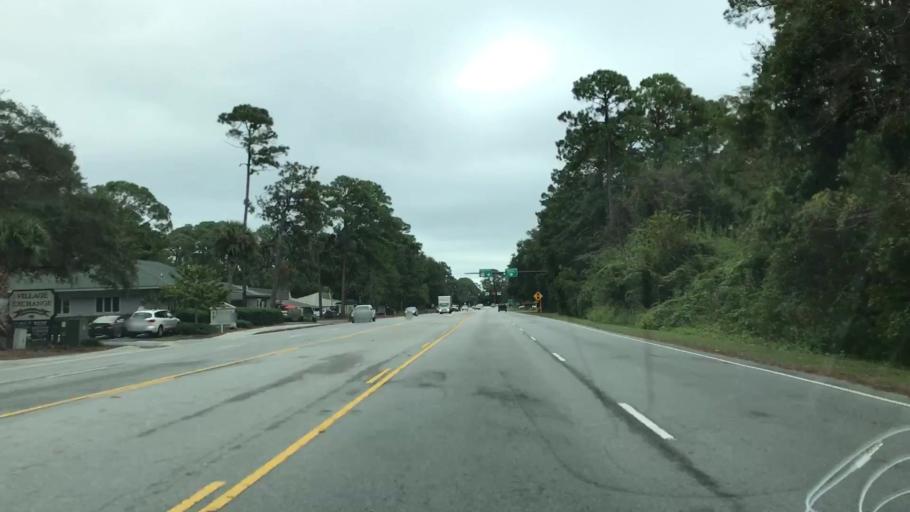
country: US
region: South Carolina
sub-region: Beaufort County
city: Hilton Head Island
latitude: 32.1602
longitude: -80.7666
